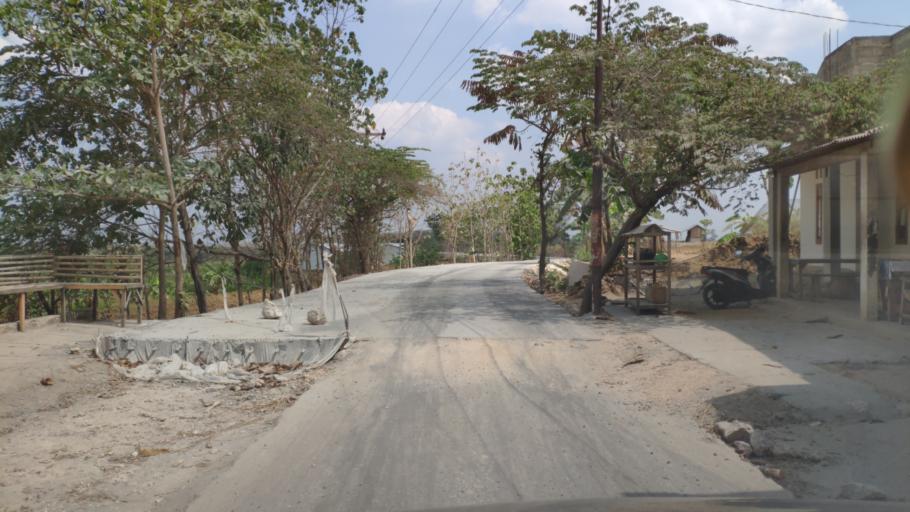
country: ID
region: Central Java
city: Ngapus
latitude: -6.9515
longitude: 111.1901
